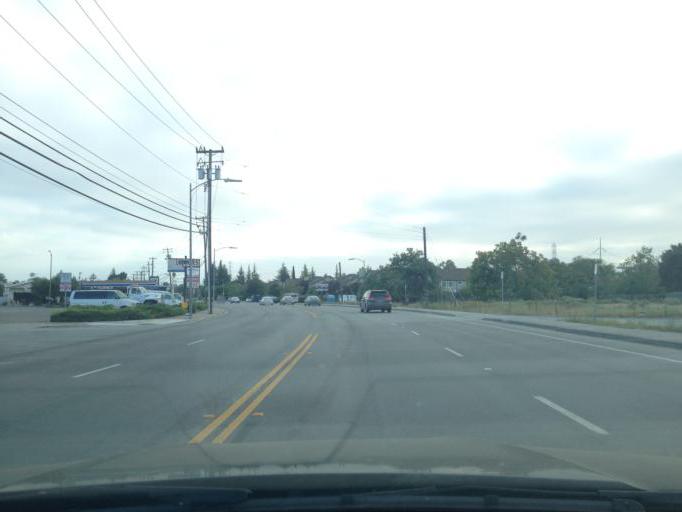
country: US
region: California
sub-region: Santa Clara County
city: Cambrian Park
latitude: 37.2309
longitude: -121.9035
